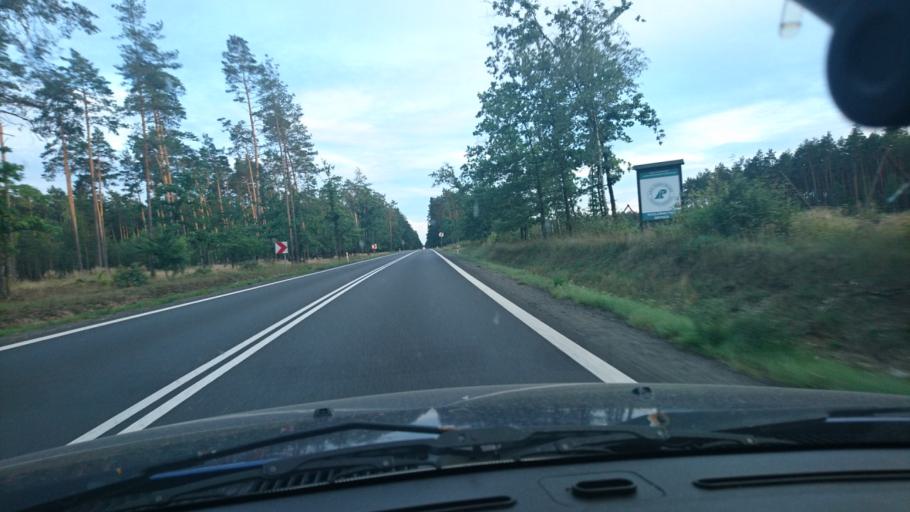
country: PL
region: Silesian Voivodeship
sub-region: Powiat tarnogorski
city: Tworog
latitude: 50.5839
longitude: 18.7070
